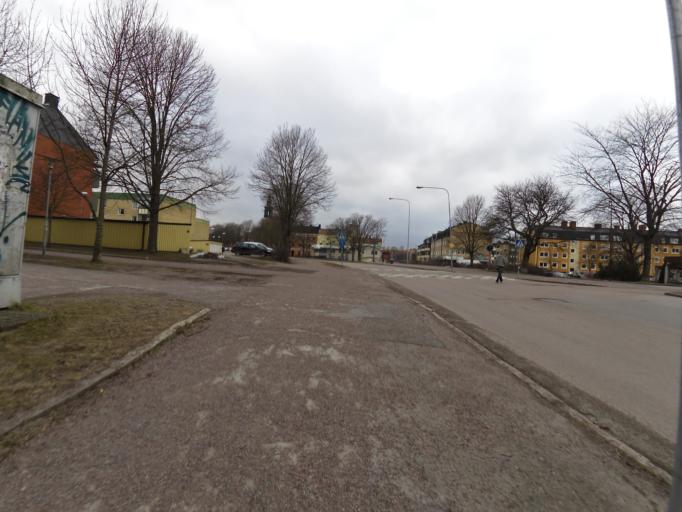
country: SE
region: Gaevleborg
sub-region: Gavle Kommun
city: Gavle
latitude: 60.6712
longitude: 17.1686
